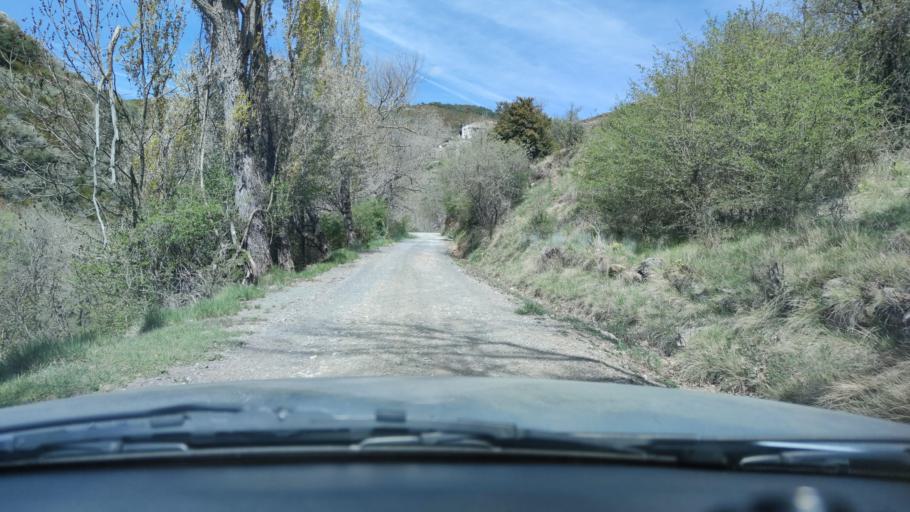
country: ES
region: Catalonia
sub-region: Provincia de Lleida
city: Sort
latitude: 42.2961
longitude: 1.1809
